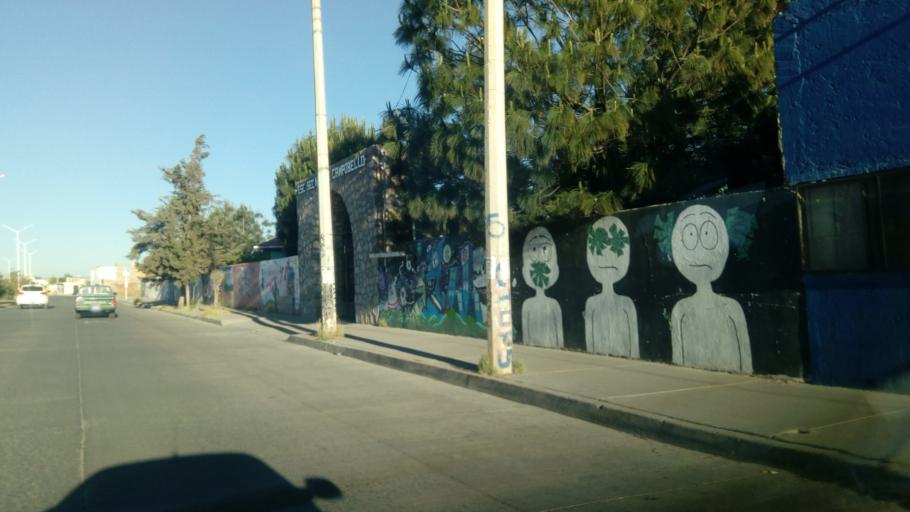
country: MX
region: Durango
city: Victoria de Durango
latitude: 24.0560
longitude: -104.5917
